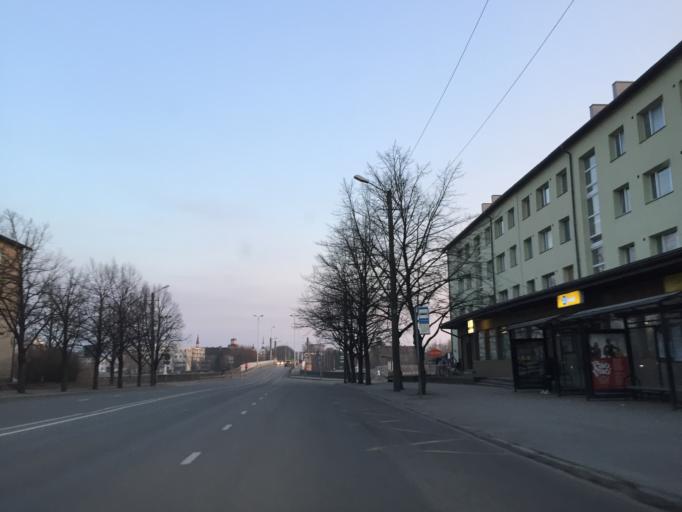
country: EE
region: Paernumaa
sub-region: Paernu linn
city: Parnu
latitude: 58.3911
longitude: 24.4952
